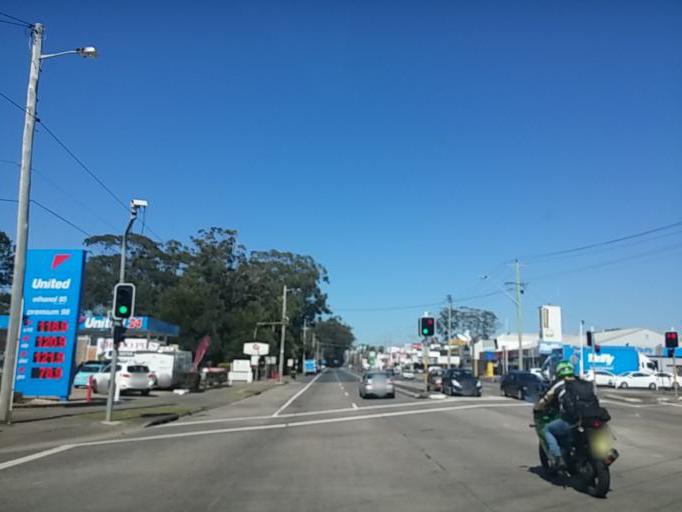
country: AU
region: New South Wales
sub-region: Coffs Harbour
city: Coffs Harbour
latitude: -30.2899
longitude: 153.1213
